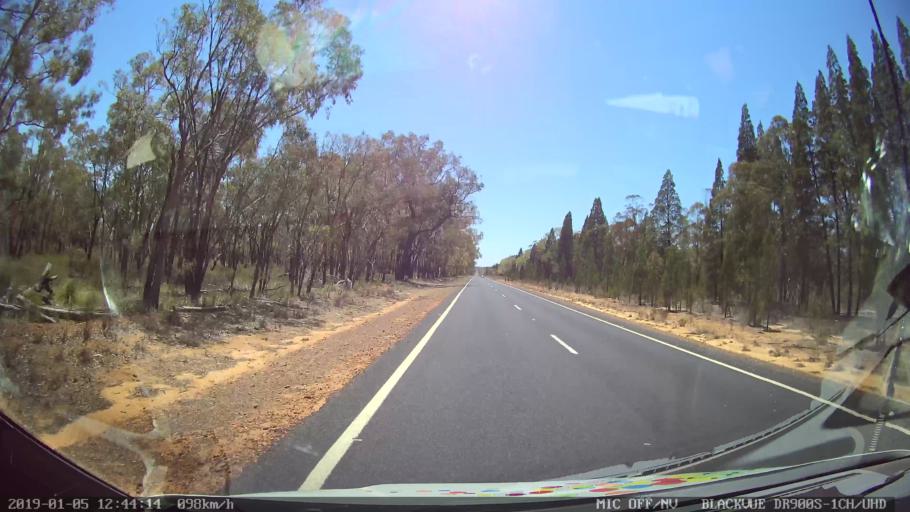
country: AU
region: New South Wales
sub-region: Warrumbungle Shire
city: Coonabarabran
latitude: -31.1397
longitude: 149.5347
